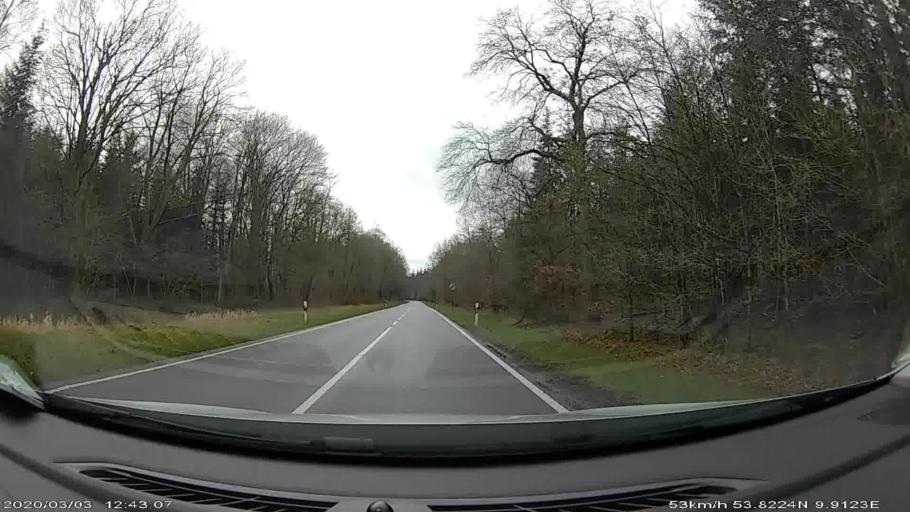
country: DE
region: Schleswig-Holstein
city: Alveslohe
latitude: 53.8214
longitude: 9.9101
